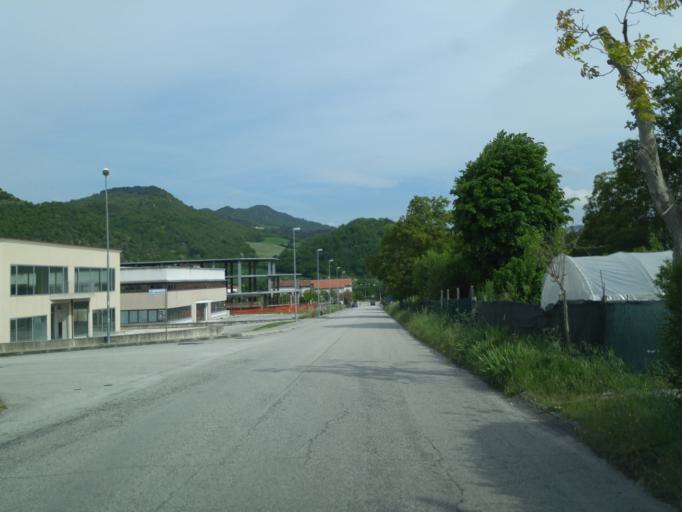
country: IT
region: The Marches
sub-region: Provincia di Pesaro e Urbino
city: Acqualagna
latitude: 43.6272
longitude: 12.6768
